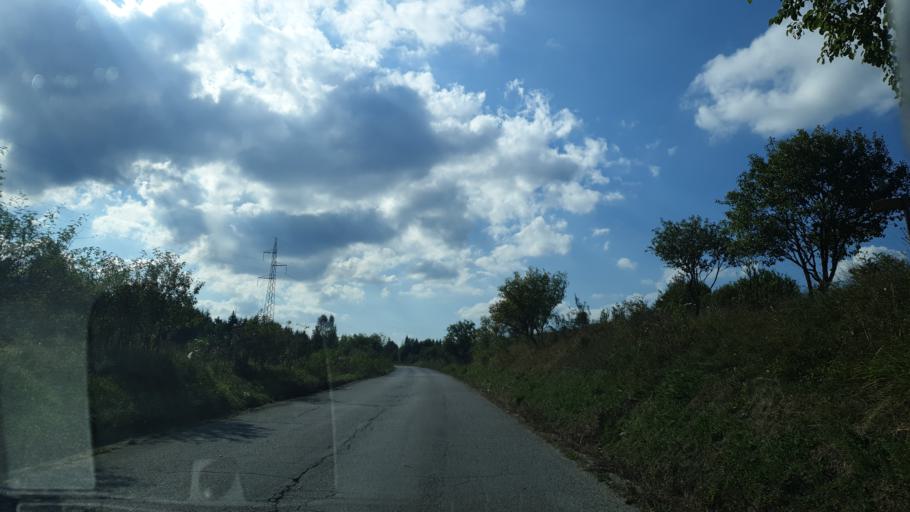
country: RS
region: Central Serbia
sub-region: Zlatiborski Okrug
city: Nova Varos
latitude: 43.4259
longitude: 19.9078
